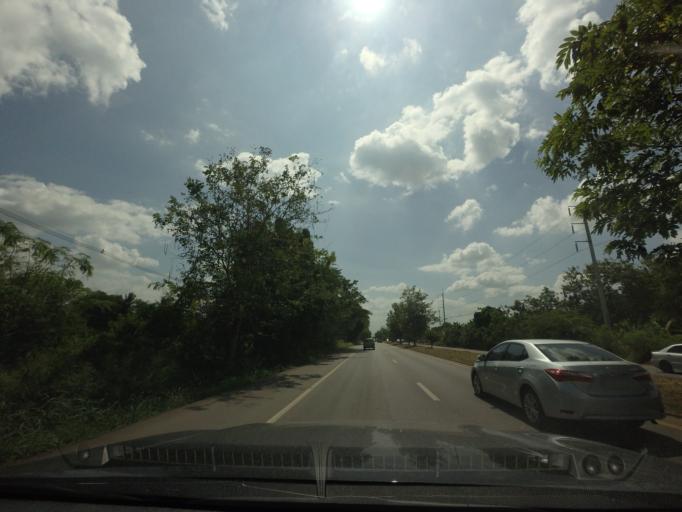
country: TH
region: Phetchabun
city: Nong Phai
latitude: 15.9571
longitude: 101.0433
